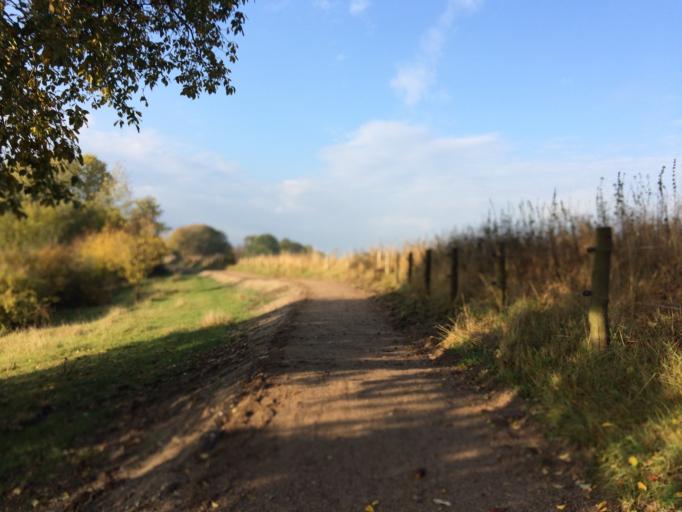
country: DK
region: Zealand
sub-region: Ringsted Kommune
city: Ringsted
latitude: 55.4872
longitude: 11.7899
